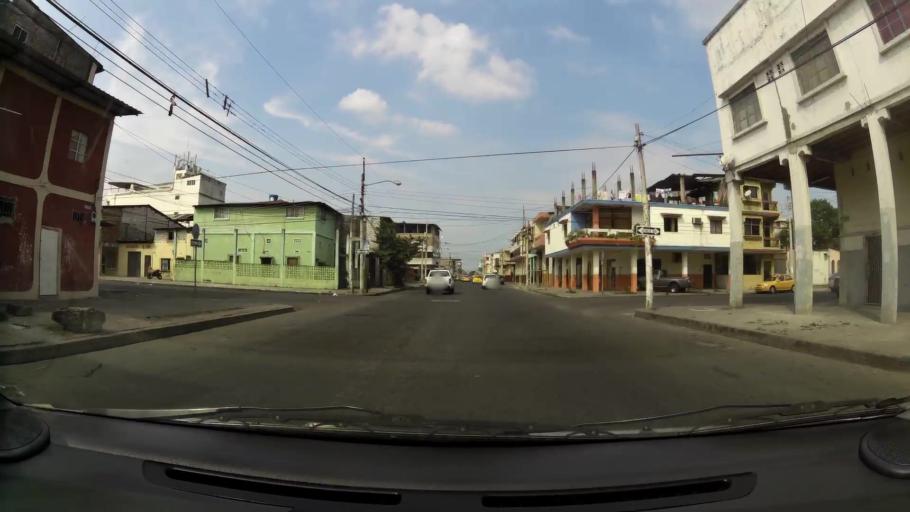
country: EC
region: Guayas
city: Guayaquil
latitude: -2.2068
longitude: -79.9024
